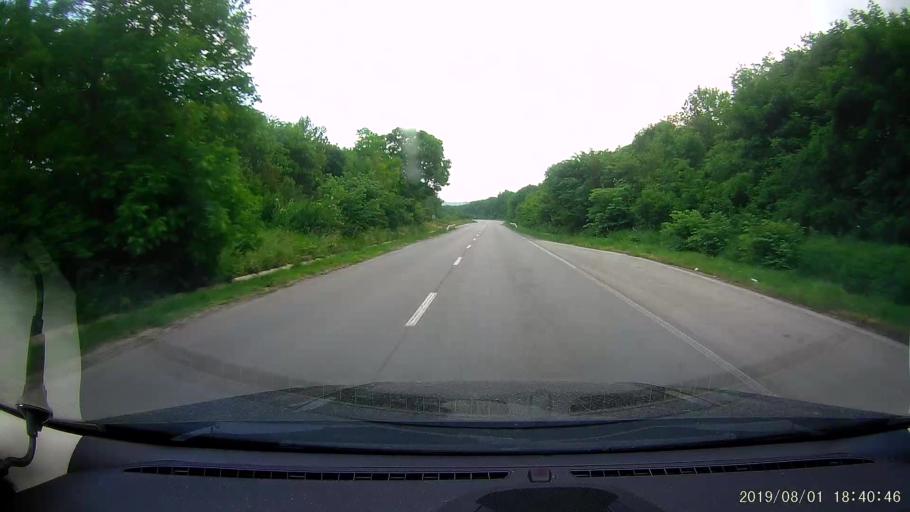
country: BG
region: Shumen
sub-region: Obshtina Khitrino
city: Gara Khitrino
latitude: 43.3592
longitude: 26.9208
